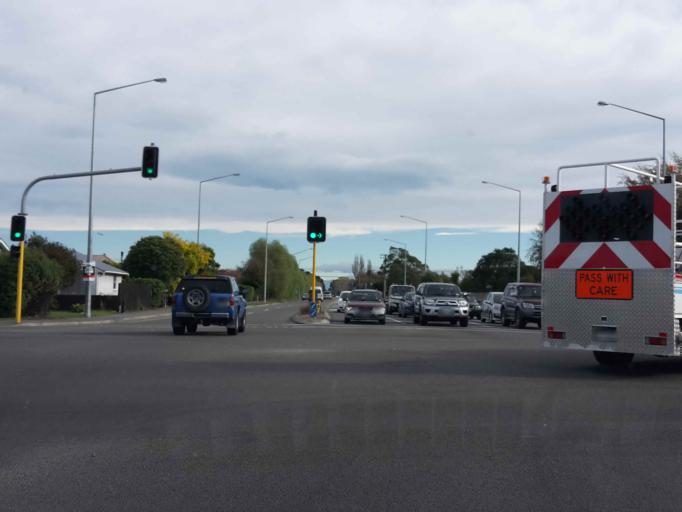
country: NZ
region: Canterbury
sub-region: Selwyn District
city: Prebbleton
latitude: -43.5204
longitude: 172.5343
